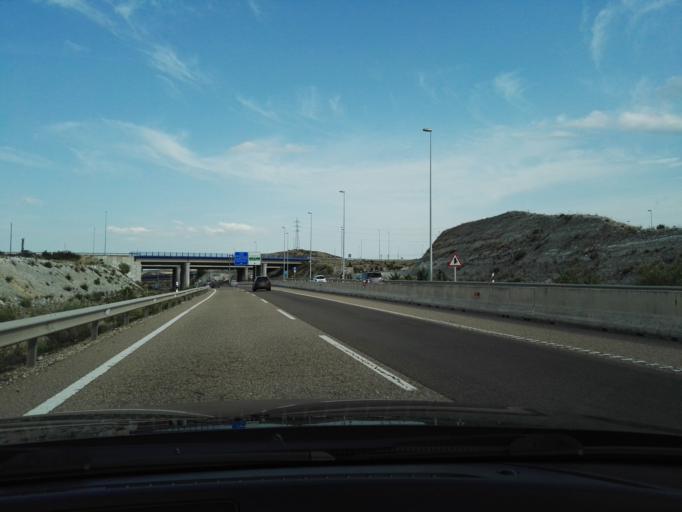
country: ES
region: Aragon
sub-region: Provincia de Zaragoza
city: Montecanal
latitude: 41.6151
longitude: -0.9343
